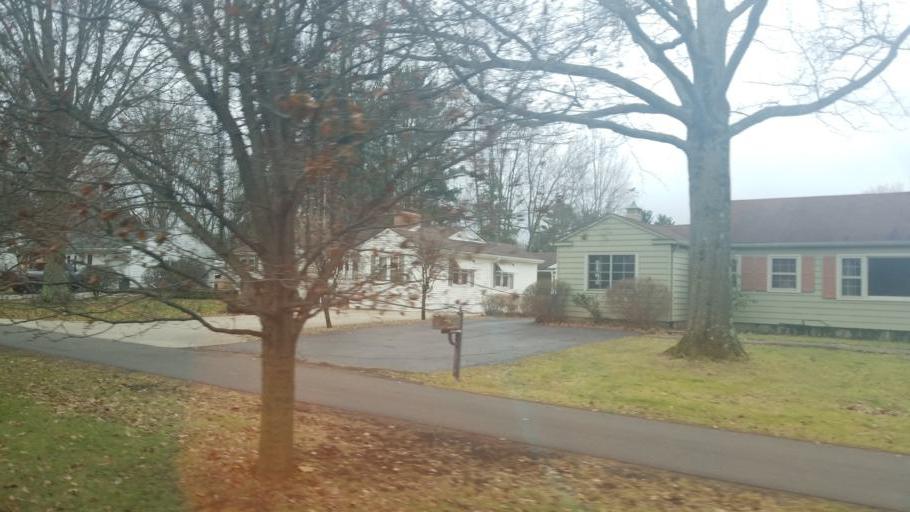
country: US
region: Ohio
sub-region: Crawford County
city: Galion
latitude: 40.7467
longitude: -82.7874
